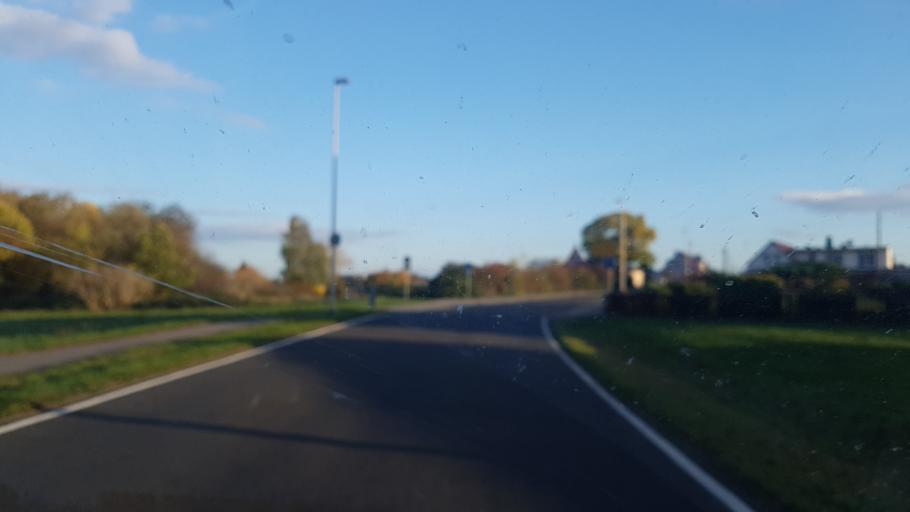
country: DE
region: Saxony
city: Oschatz
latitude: 51.3130
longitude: 13.0918
